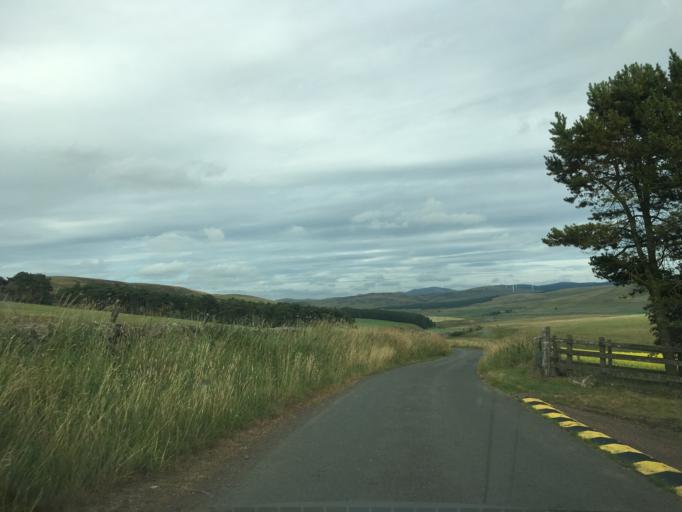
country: GB
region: Scotland
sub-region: South Lanarkshire
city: Douglas
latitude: 55.5127
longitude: -3.7278
